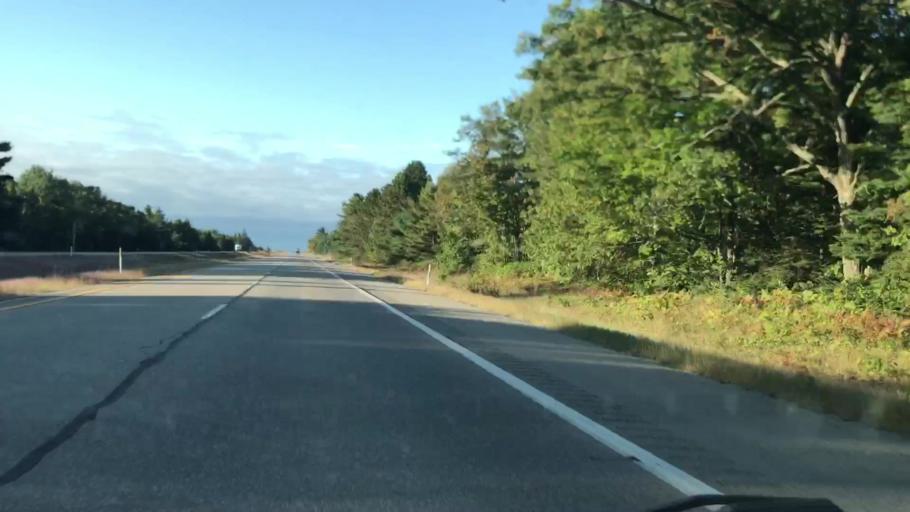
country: US
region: Michigan
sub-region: Chippewa County
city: Sault Ste. Marie
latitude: 46.4334
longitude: -84.3898
